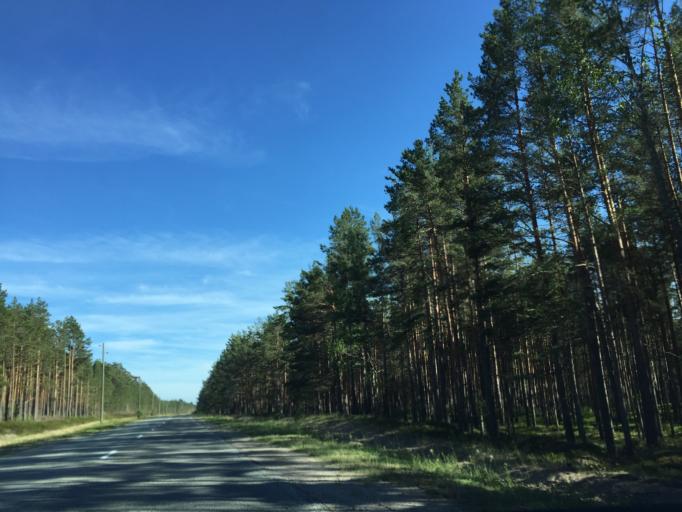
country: LV
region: Mesraga
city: Mersrags
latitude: 57.3192
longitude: 23.1350
